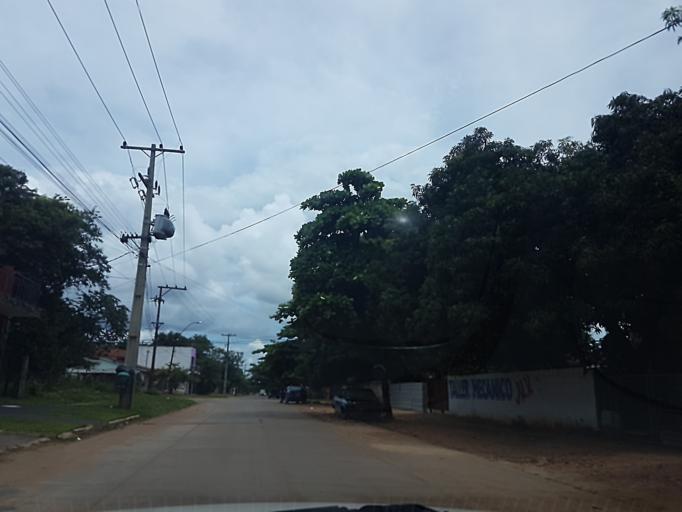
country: PY
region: Central
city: Limpio
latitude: -25.1716
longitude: -57.4739
